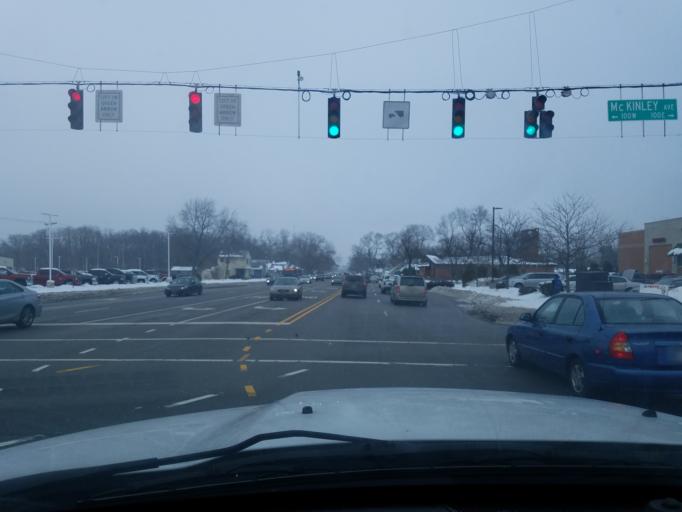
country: US
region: Indiana
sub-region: Saint Joseph County
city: Mishawaka
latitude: 41.6805
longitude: -86.1814
